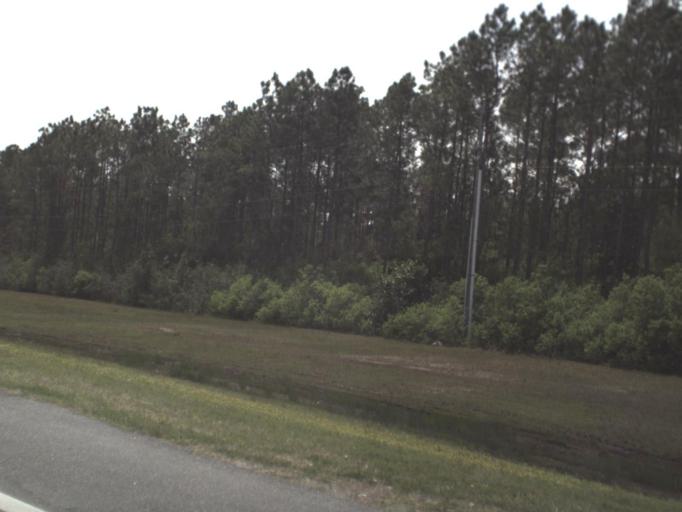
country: US
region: Florida
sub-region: Escambia County
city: Myrtle Grove
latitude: 30.4071
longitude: -87.3423
